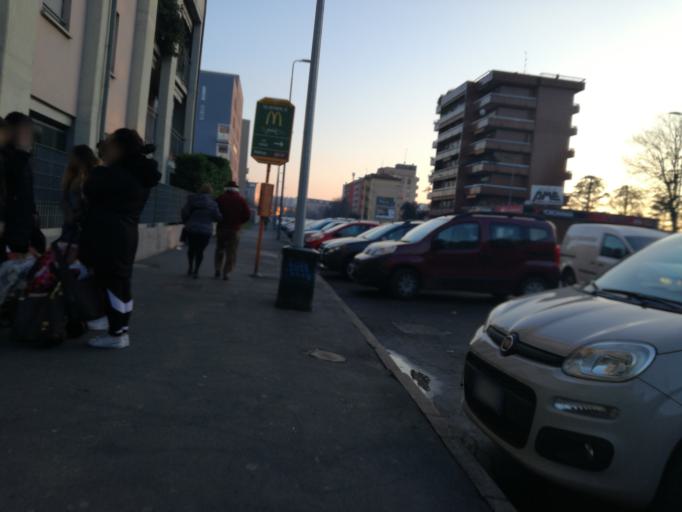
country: IT
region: Lombardy
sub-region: Citta metropolitana di Milano
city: Romano Banco
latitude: 45.4356
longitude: 9.1546
